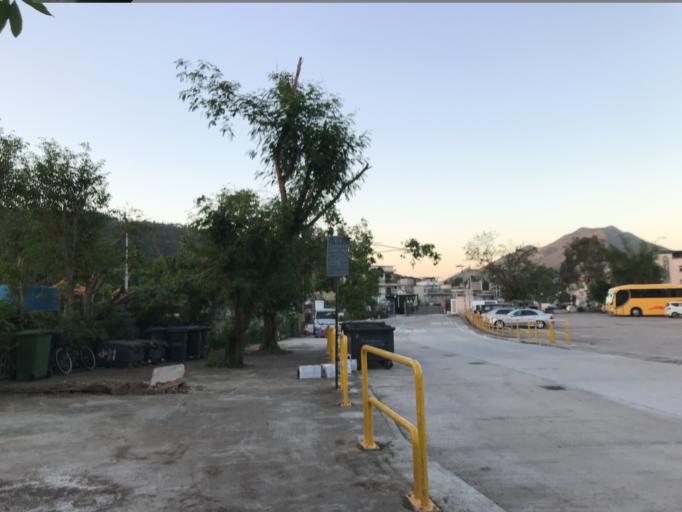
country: HK
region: Tai Po
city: Tai Po
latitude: 22.4675
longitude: 114.1502
